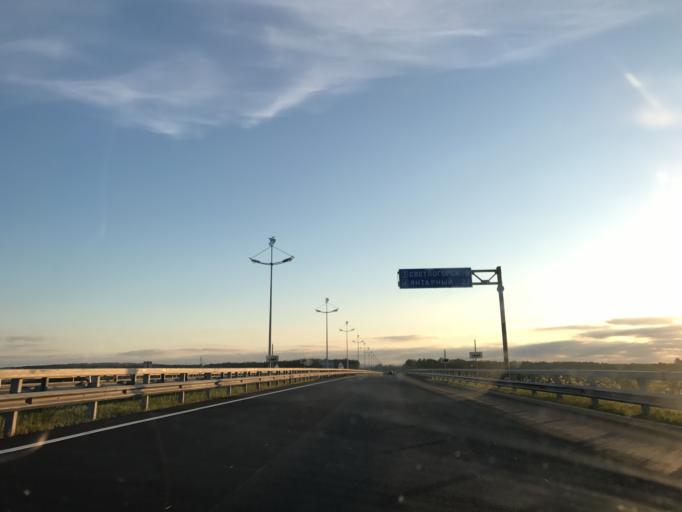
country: RU
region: Kaliningrad
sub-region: Gorod Kaliningrad
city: Pionerskiy
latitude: 54.9201
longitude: 20.2672
